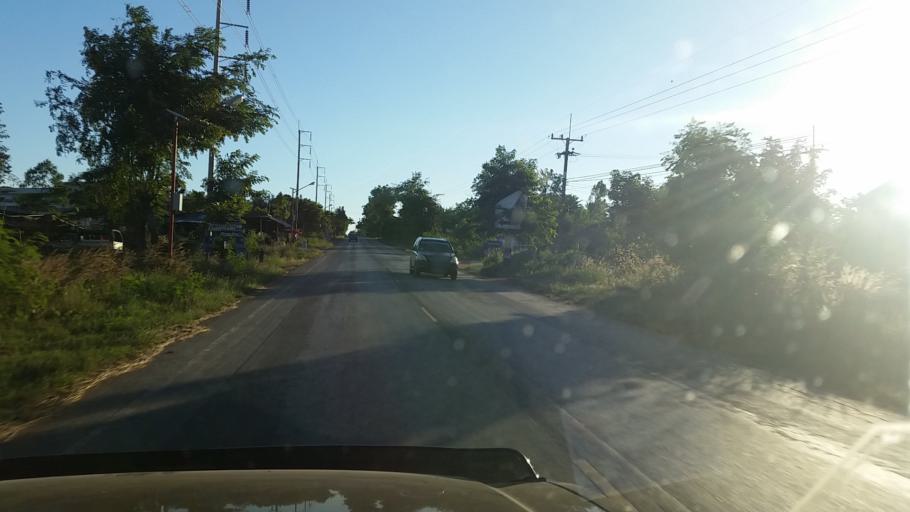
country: TH
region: Chaiyaphum
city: Nong Bua Rawe
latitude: 15.7244
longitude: 101.7444
